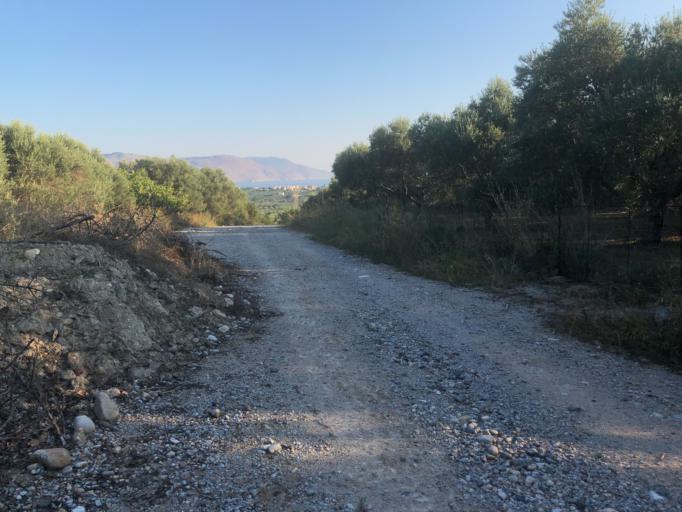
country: GR
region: Crete
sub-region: Nomos Chanias
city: Georgioupolis
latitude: 35.3363
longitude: 24.2904
